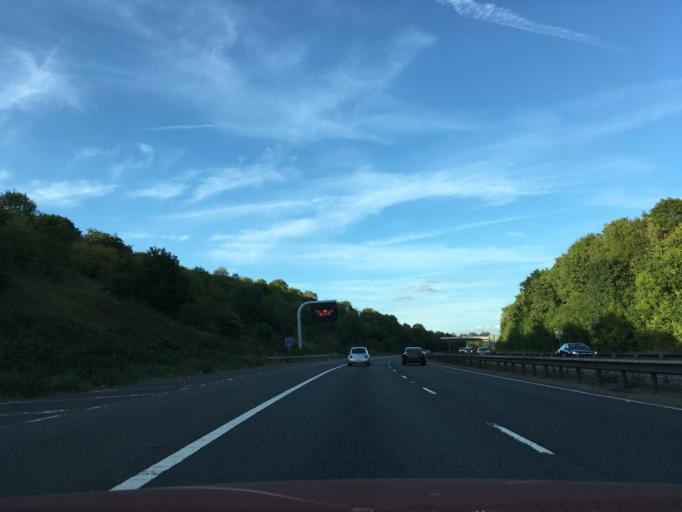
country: GB
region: England
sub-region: South Gloucestershire
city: Stoke Gifford
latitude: 51.4842
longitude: -2.5587
